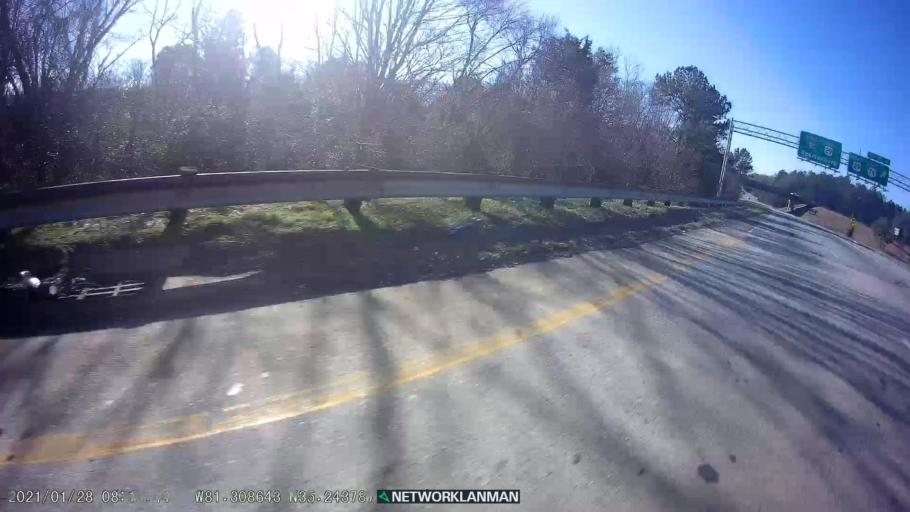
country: US
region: North Carolina
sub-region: Cleveland County
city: Kings Mountain
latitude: 35.2438
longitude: -81.3091
